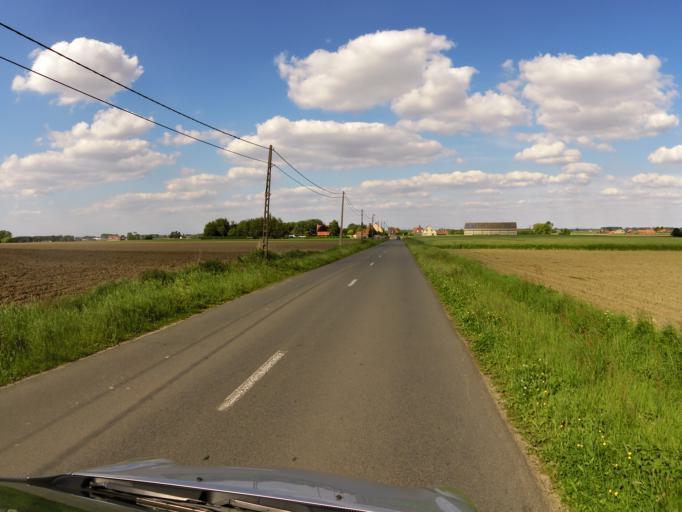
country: BE
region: Flanders
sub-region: Provincie West-Vlaanderen
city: Poperinge
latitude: 50.8729
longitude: 2.7392
